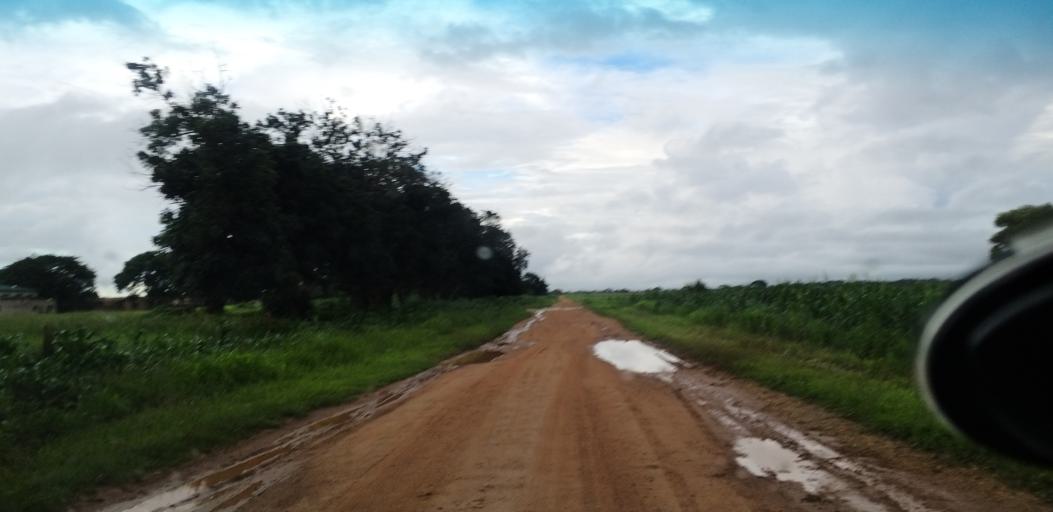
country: ZM
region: Lusaka
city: Lusaka
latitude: -15.5234
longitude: 28.2978
